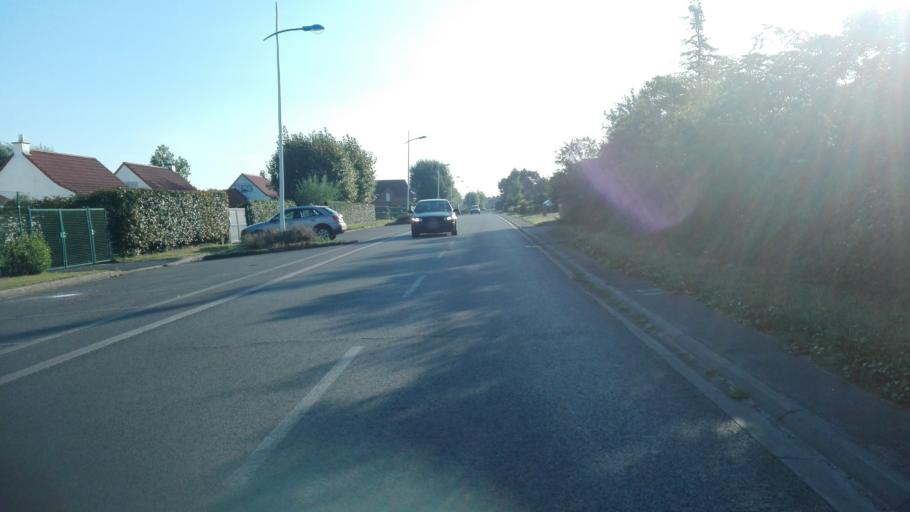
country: FR
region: Nord-Pas-de-Calais
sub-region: Departement du Nord
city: Ghyvelde
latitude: 51.0508
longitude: 2.5094
